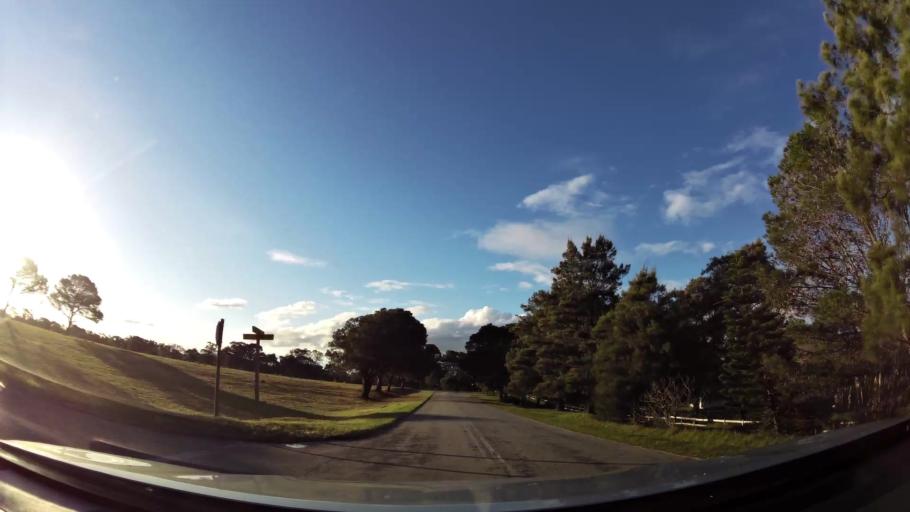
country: ZA
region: Eastern Cape
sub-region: Nelson Mandela Bay Metropolitan Municipality
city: Port Elizabeth
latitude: -33.9763
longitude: 25.4837
